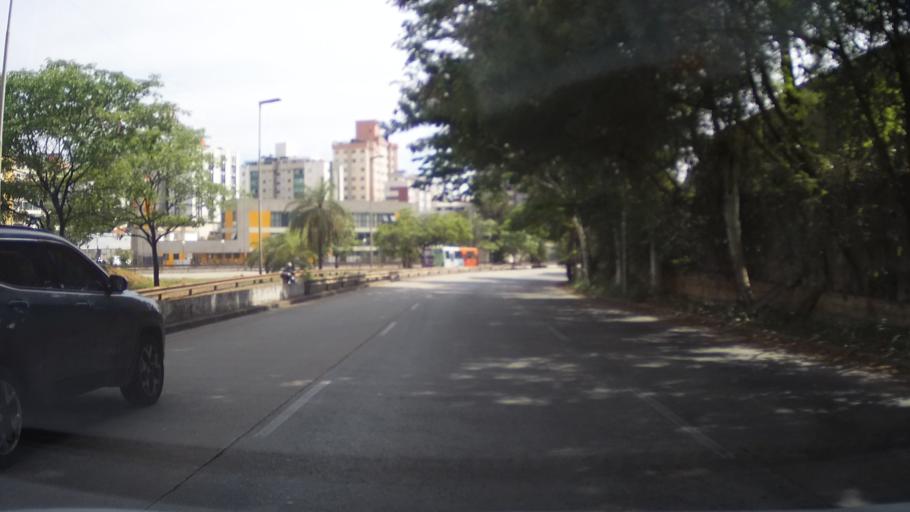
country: BR
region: Minas Gerais
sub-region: Belo Horizonte
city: Belo Horizonte
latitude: -19.9291
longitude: -43.9910
